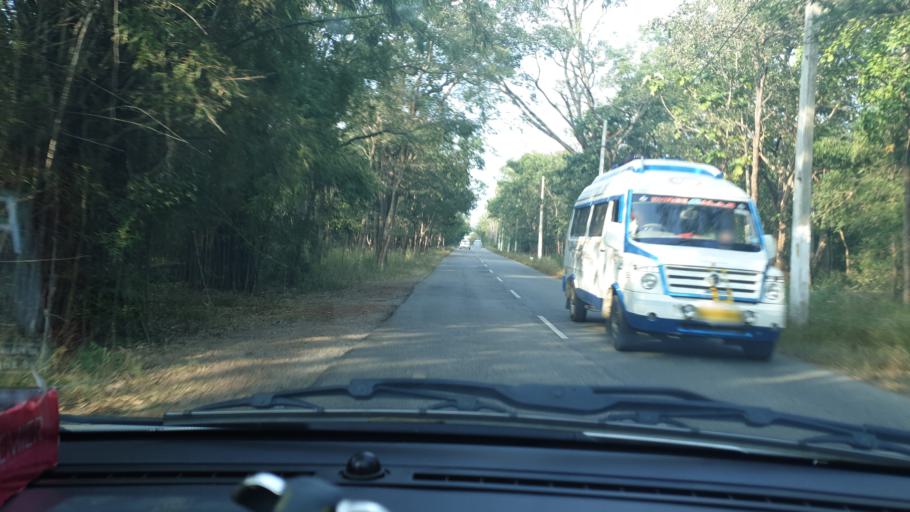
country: IN
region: Andhra Pradesh
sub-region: Kurnool
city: Srisailam
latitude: 16.2988
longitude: 78.7312
